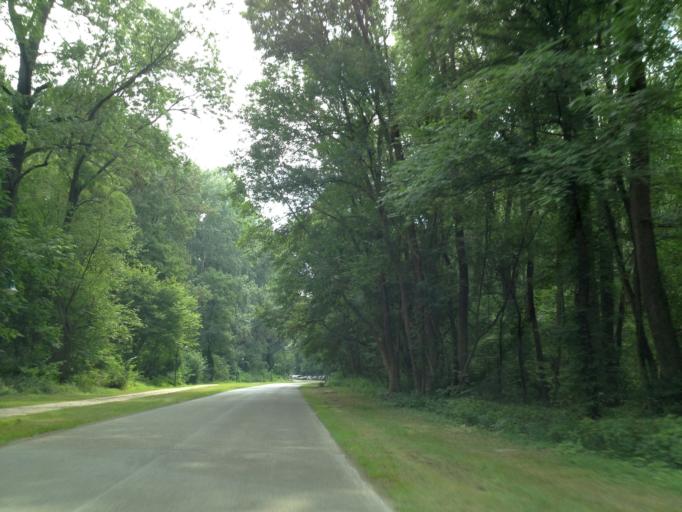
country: AT
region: Lower Austria
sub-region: Politischer Bezirk Ganserndorf
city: Orth an der Donau
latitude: 48.1274
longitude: 16.7098
